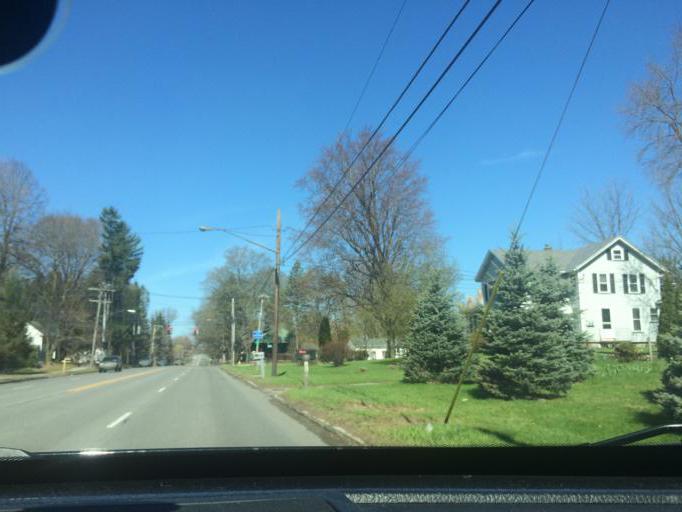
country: US
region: New York
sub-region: Monroe County
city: East Rochester
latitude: 43.1047
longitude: -77.4880
